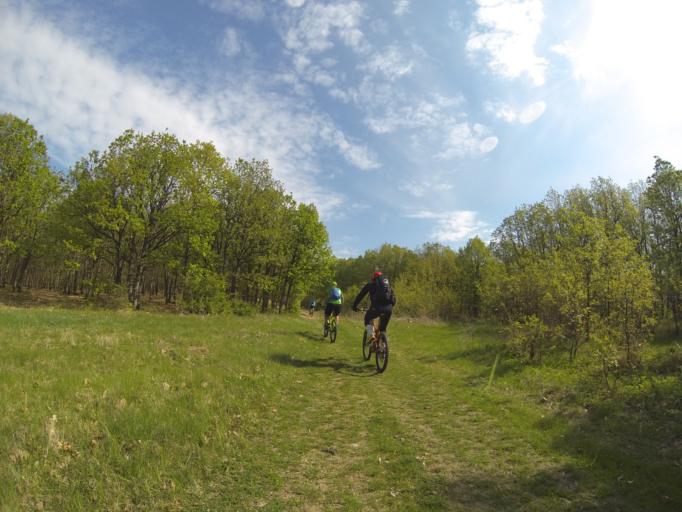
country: RO
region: Dolj
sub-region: Comuna Bradesti
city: Bradesti
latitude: 44.5216
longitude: 23.6128
